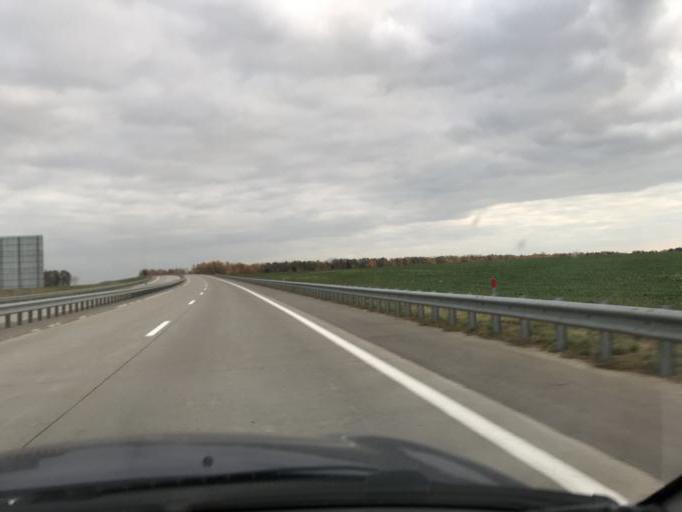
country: BY
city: Fanipol
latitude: 53.7714
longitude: 27.3618
